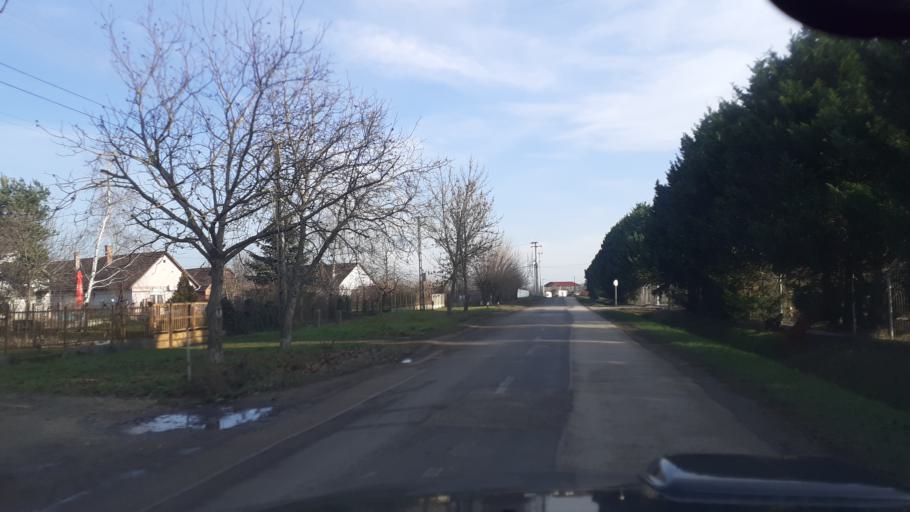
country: HU
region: Pest
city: Domsod
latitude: 47.0893
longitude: 19.0316
